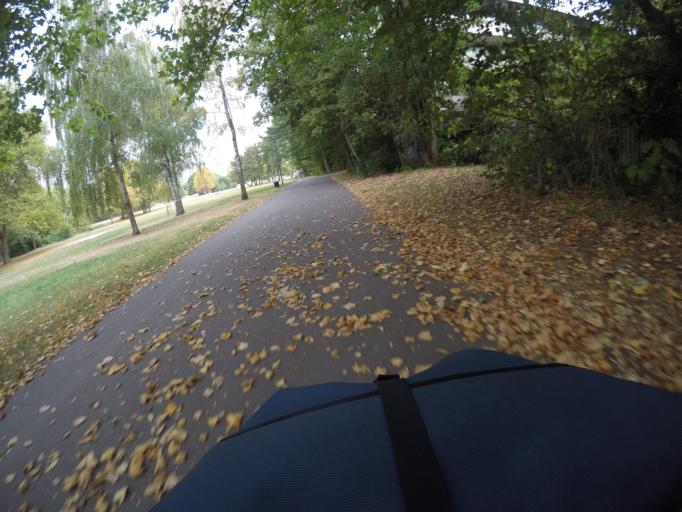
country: DE
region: North Rhine-Westphalia
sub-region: Regierungsbezirk Koln
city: Riehl
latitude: 50.9624
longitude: 6.9647
